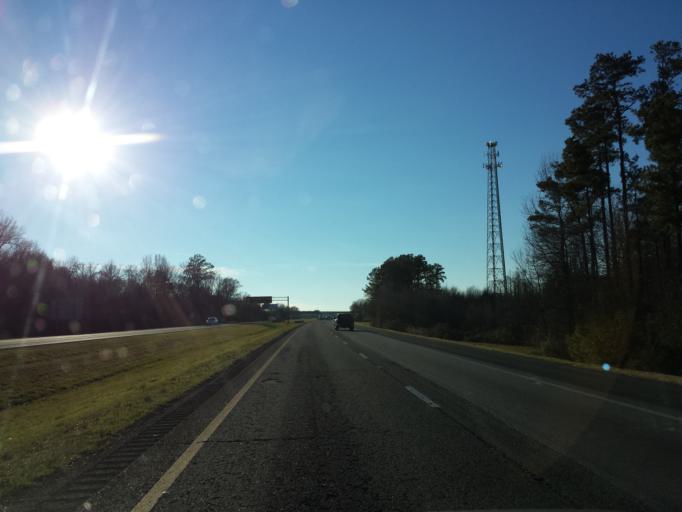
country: US
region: Alabama
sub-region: Tuscaloosa County
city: Tuscaloosa
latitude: 33.1577
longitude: -87.5818
